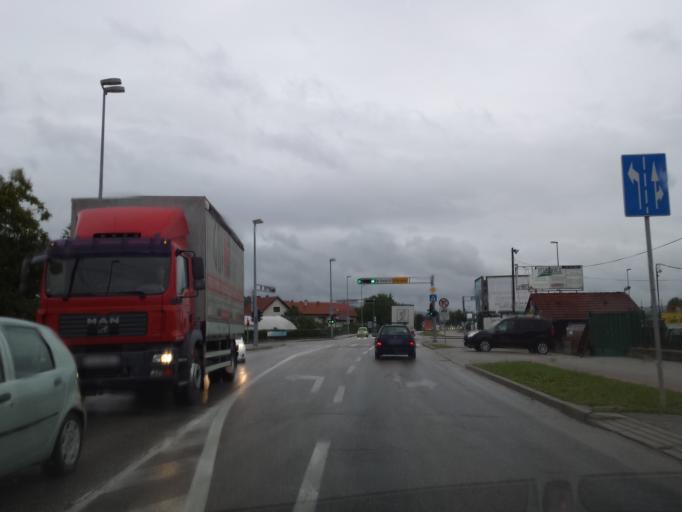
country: HR
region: Zagrebacka
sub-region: Grad Samobor
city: Samobor
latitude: 45.8066
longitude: 15.7172
